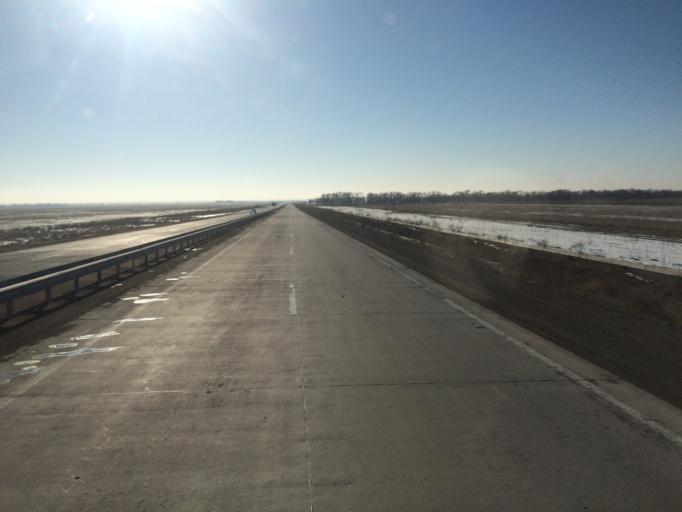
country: KG
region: Chuy
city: Sokuluk
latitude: 43.3014
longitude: 74.2525
